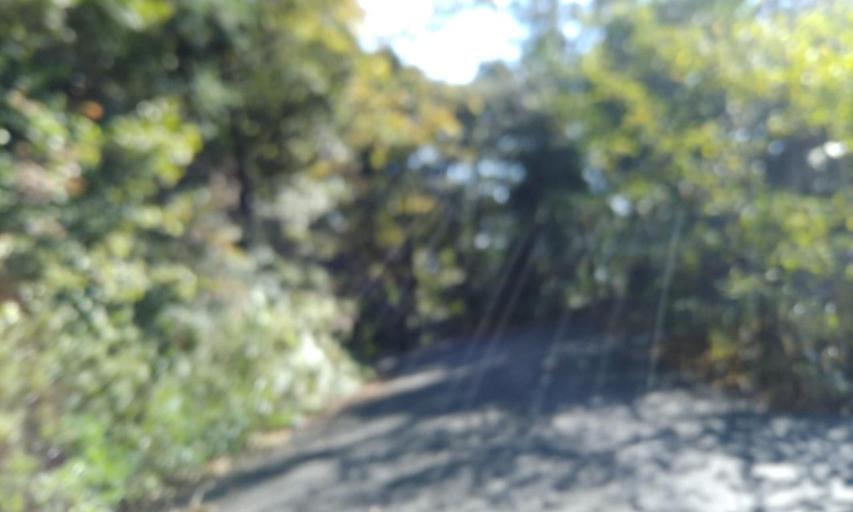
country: JP
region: Shizuoka
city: Hamakita
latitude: 34.8185
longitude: 137.6427
